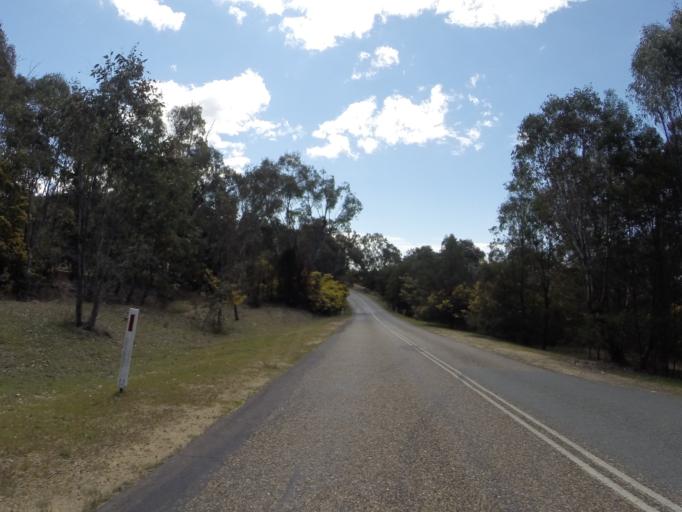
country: AU
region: Australian Capital Territory
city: Macquarie
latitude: -35.3408
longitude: 148.9304
